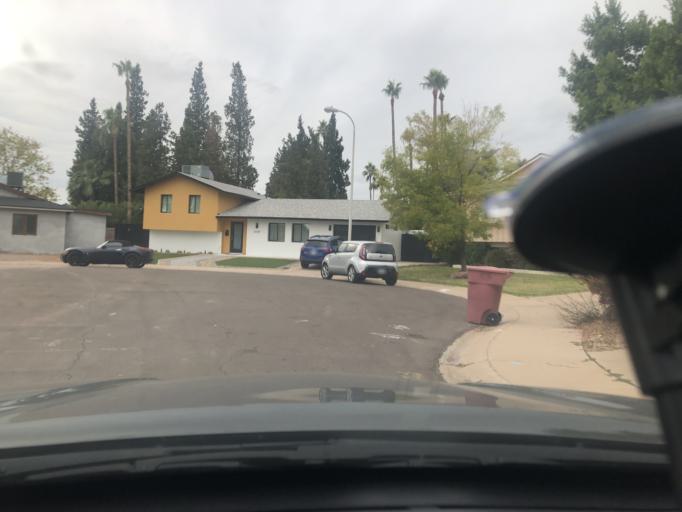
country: US
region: Arizona
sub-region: Maricopa County
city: Scottsdale
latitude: 33.4861
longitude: -111.8949
